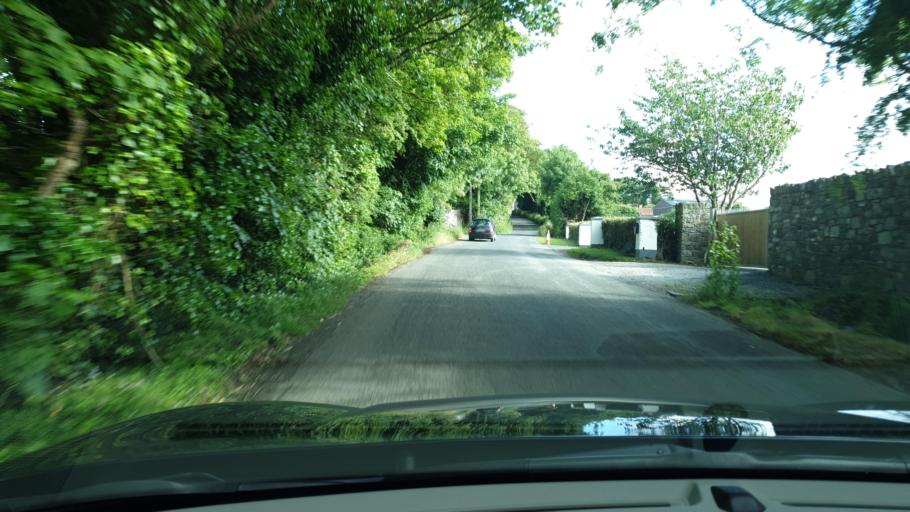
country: IE
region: Leinster
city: Balrothery
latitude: 53.5697
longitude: -6.2000
